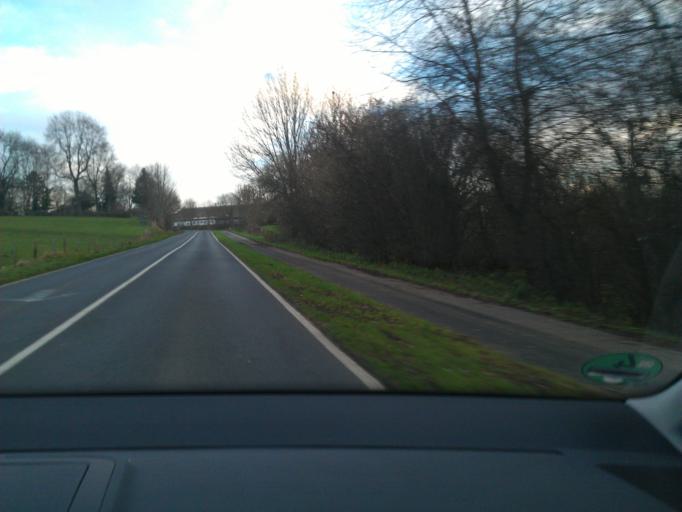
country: DE
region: North Rhine-Westphalia
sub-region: Regierungsbezirk Koln
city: Roetgen
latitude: 50.7116
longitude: 6.1703
